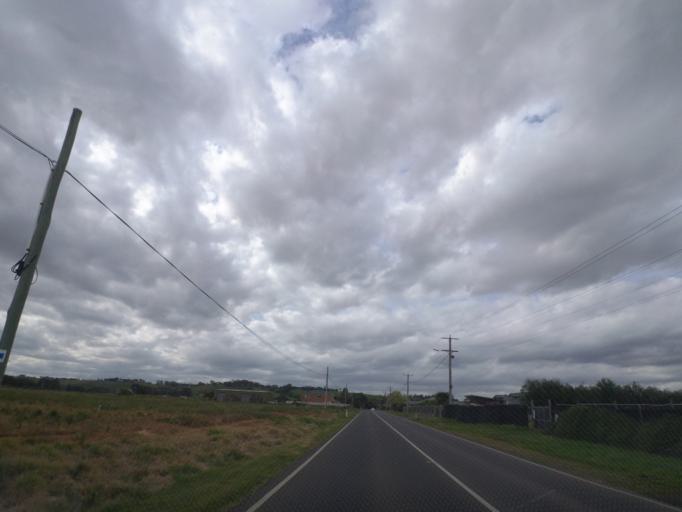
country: AU
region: Victoria
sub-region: Brimbank
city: Keilor
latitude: -37.7099
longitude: 144.8316
